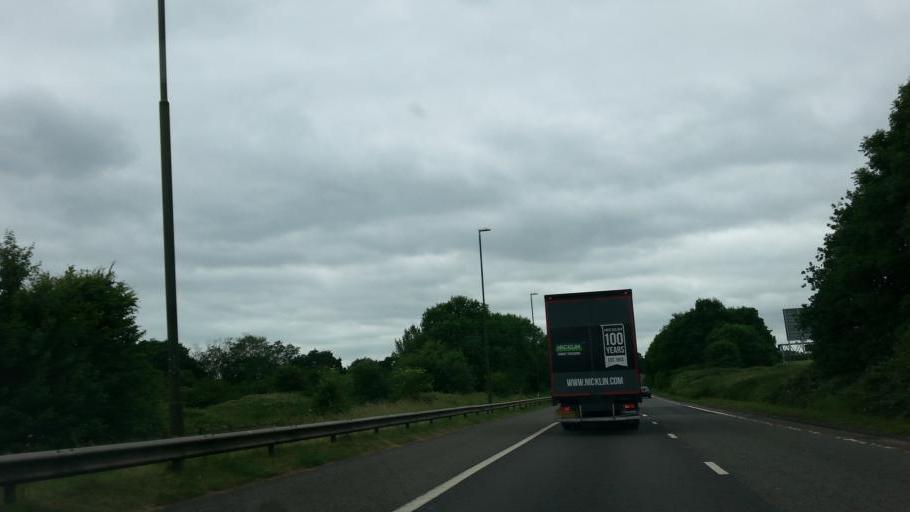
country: GB
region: England
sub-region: Warwickshire
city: Water Orton
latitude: 52.5079
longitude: -1.7317
